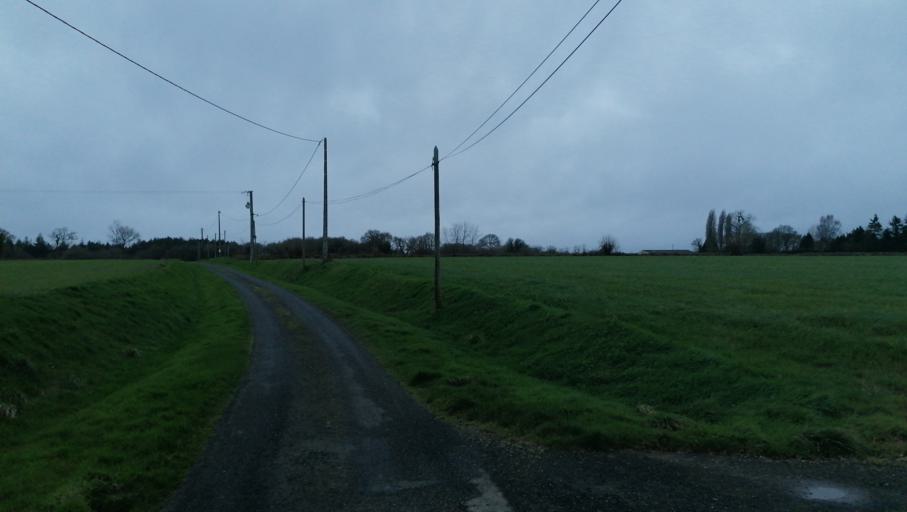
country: FR
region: Brittany
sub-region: Departement des Cotes-d'Armor
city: Lanrodec
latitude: 48.5632
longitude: -3.0484
